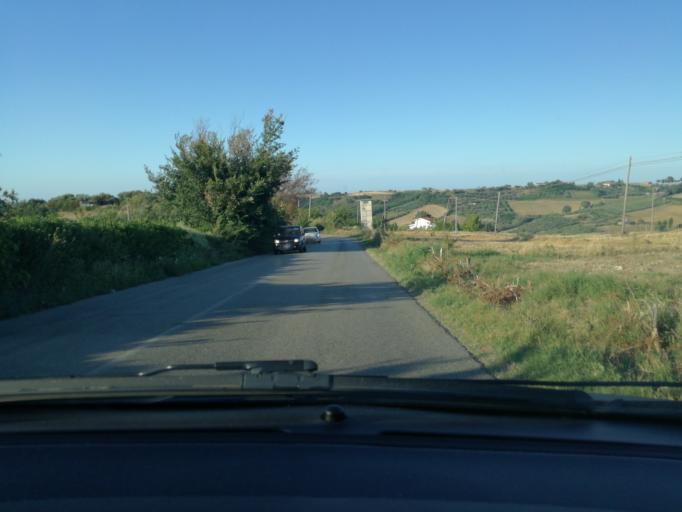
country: IT
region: Molise
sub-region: Provincia di Campobasso
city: Guglionesi
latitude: 41.9317
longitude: 14.9307
